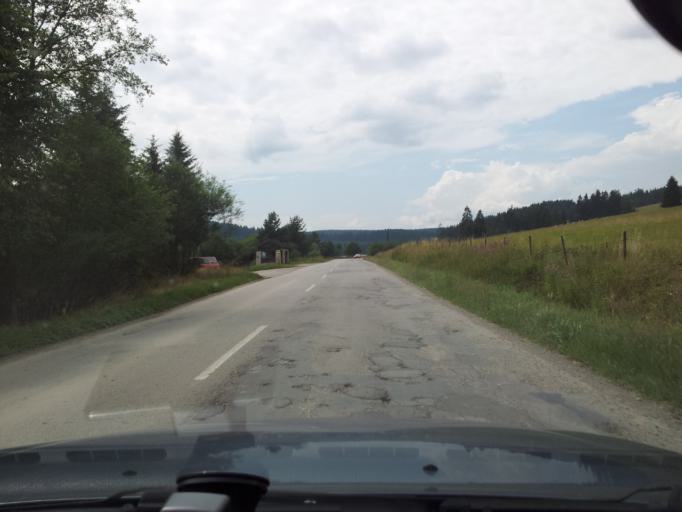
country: SK
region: Zilinsky
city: Oravska Lesna
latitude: 49.3785
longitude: 19.2740
